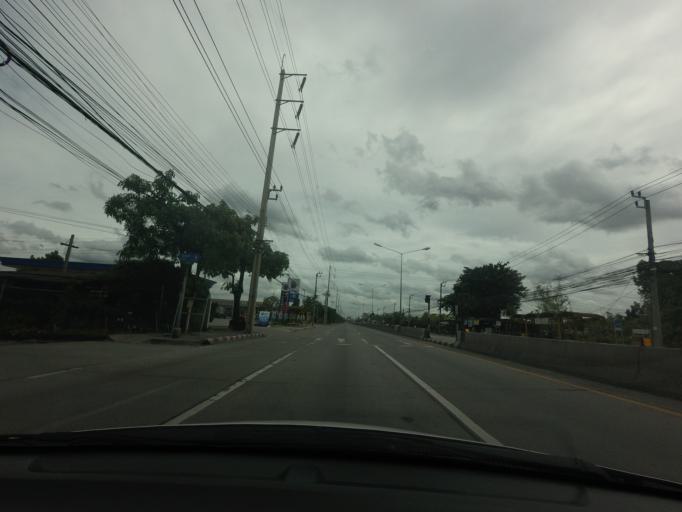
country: TH
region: Bangkok
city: Min Buri
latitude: 13.7861
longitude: 100.7463
